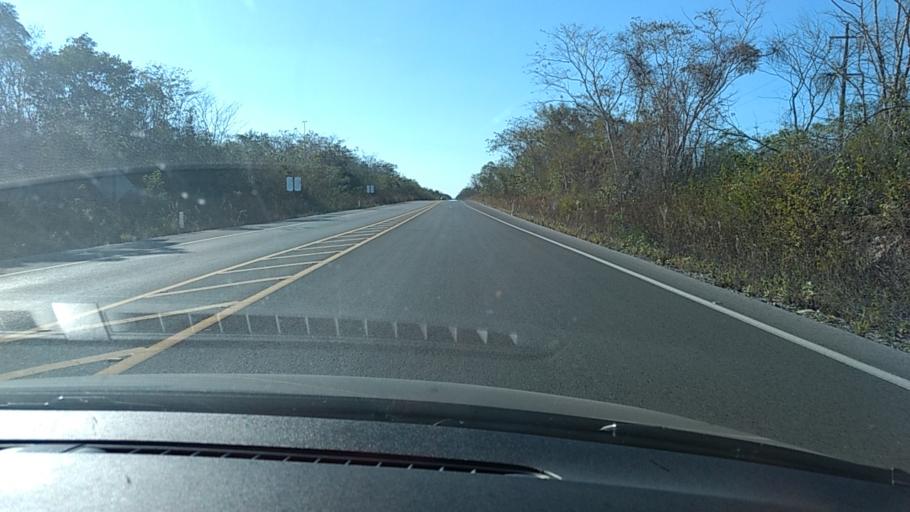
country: MX
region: Yucatan
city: Chichen-Itza
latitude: 20.6390
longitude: -88.4789
